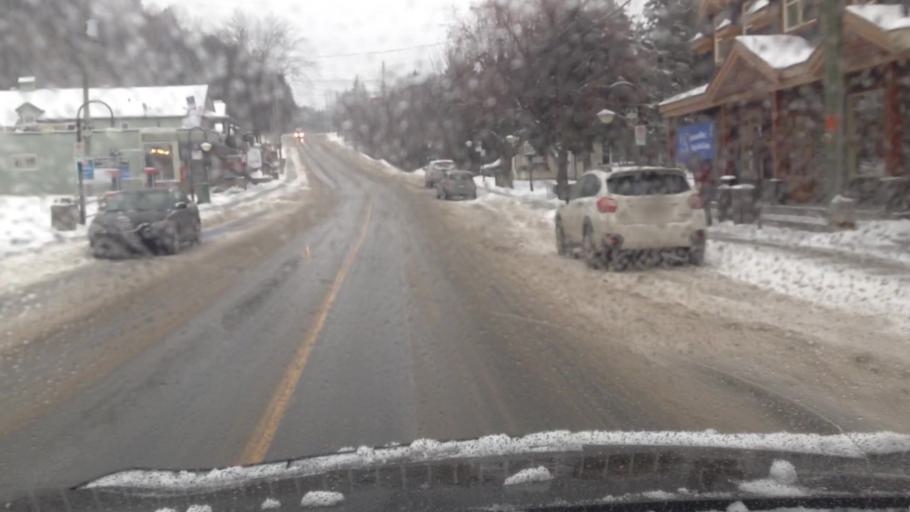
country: CA
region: Quebec
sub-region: Laurentides
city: Mont-Tremblant
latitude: 46.1187
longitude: -74.5886
